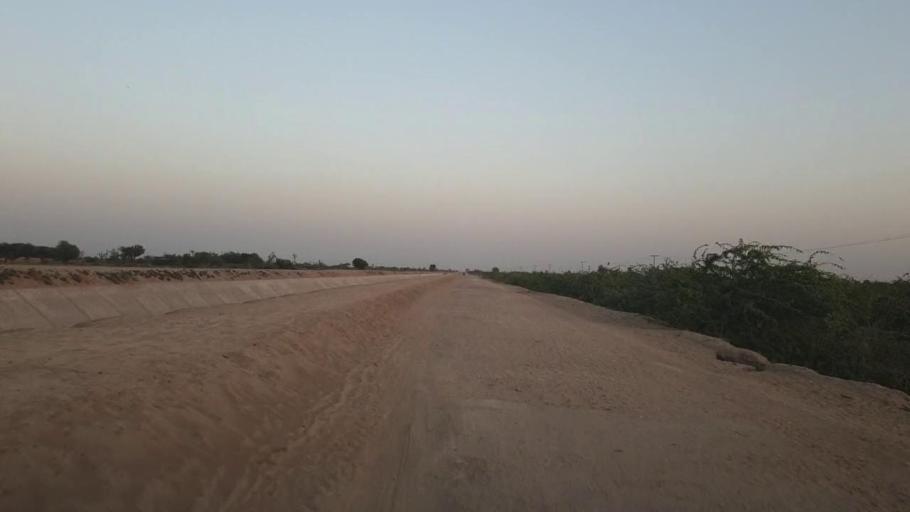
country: PK
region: Sindh
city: Dhoro Naro
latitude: 25.4421
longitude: 69.6347
